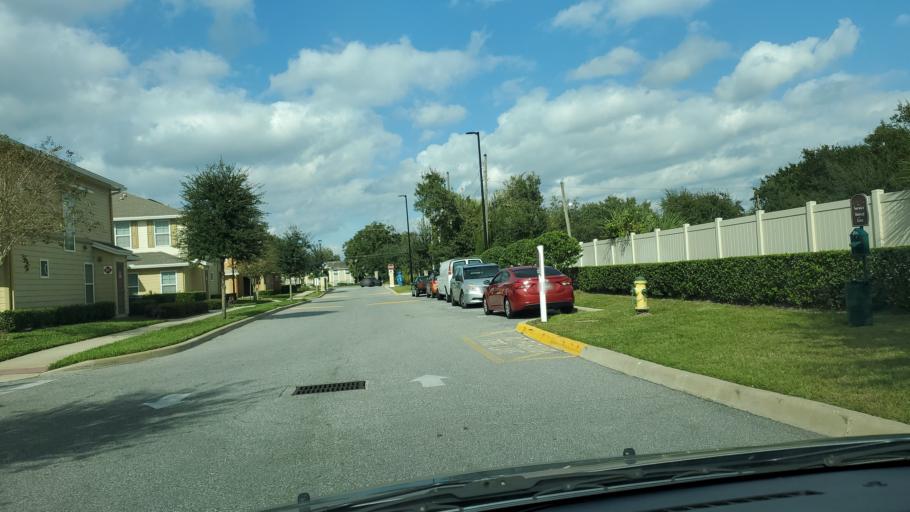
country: US
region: Florida
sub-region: Orange County
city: Conway
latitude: 28.4979
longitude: -81.2958
